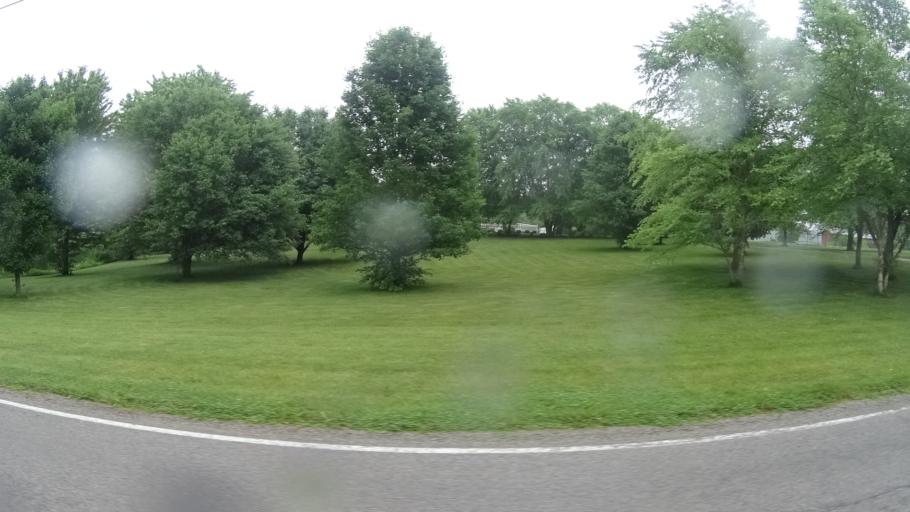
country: US
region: Ohio
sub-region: Huron County
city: Bellevue
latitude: 41.3694
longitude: -82.8450
